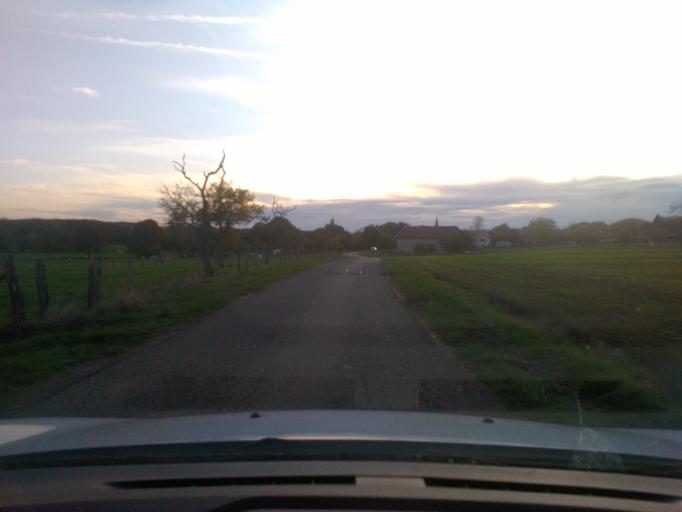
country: FR
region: Lorraine
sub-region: Departement des Vosges
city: Mirecourt
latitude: 48.3984
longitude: 6.1402
